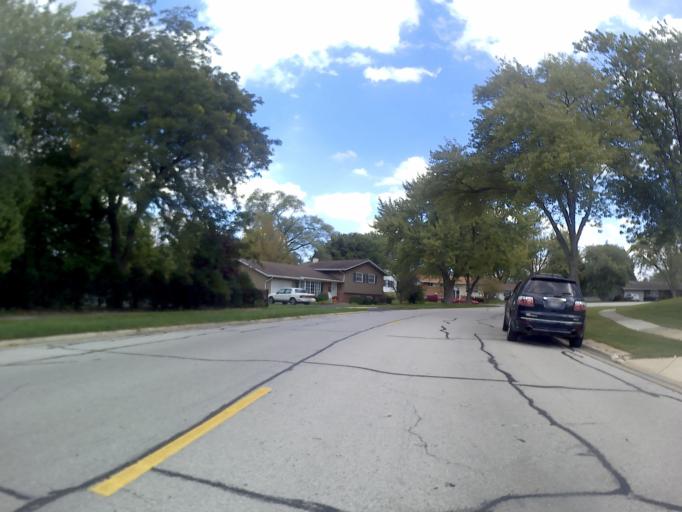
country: US
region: Illinois
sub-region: DuPage County
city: Woodridge
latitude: 41.7693
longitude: -88.0639
